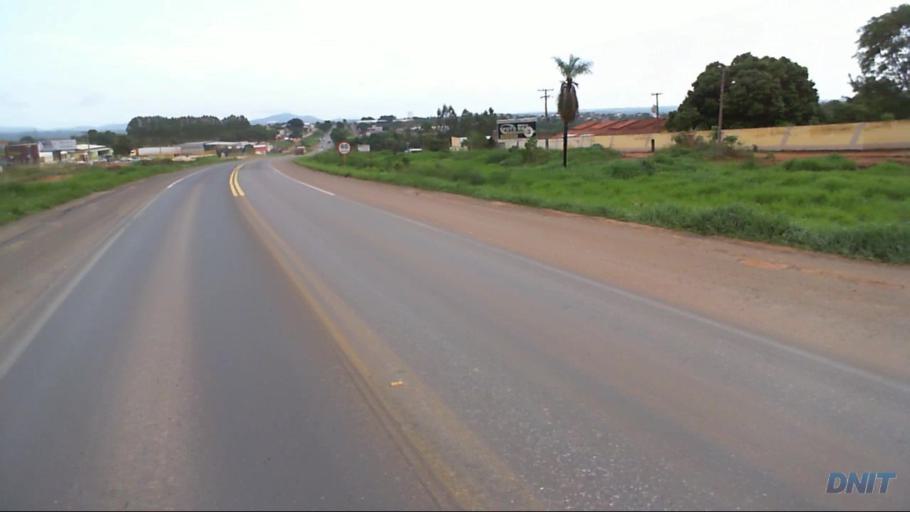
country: BR
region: Goias
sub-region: Uruacu
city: Uruacu
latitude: -14.5402
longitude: -49.1622
